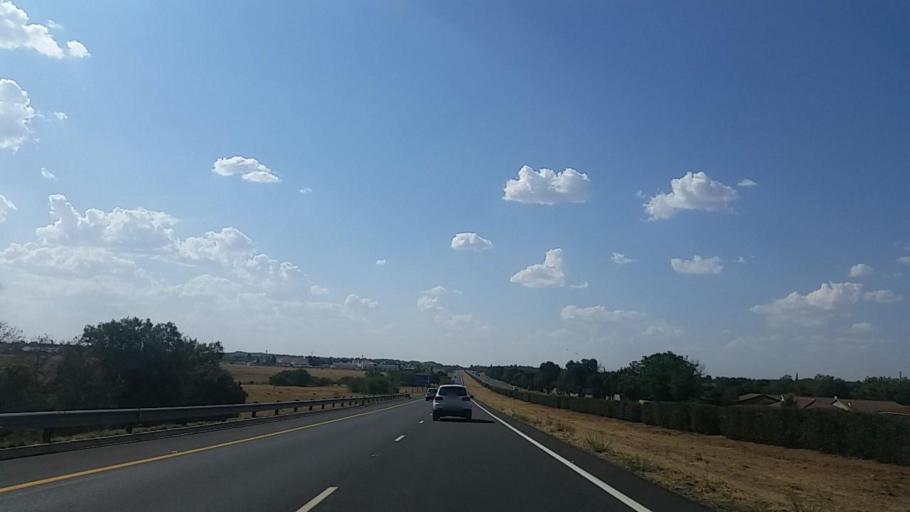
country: ZA
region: Orange Free State
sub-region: Mangaung Metropolitan Municipality
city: Bloemfontein
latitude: -29.1782
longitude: 26.1886
